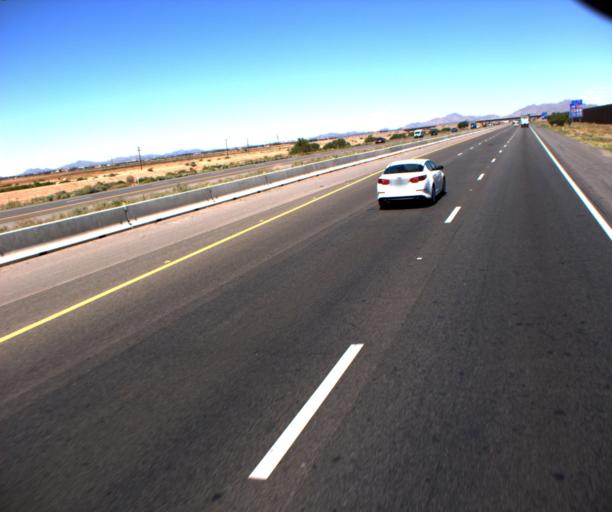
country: US
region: Arizona
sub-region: Pinal County
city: Casa Grande
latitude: 32.8582
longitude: -111.6870
